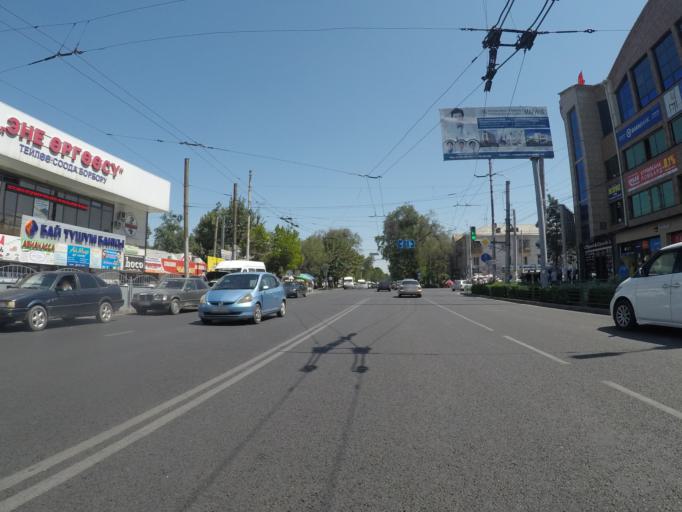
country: KG
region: Chuy
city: Bishkek
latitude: 42.8774
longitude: 74.5710
